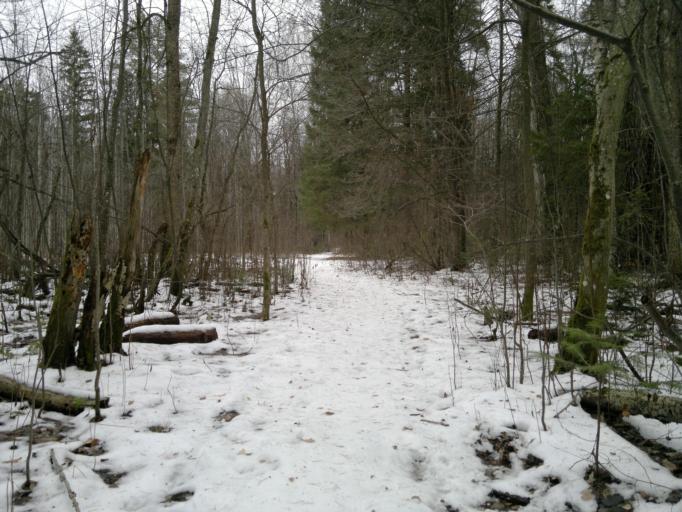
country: RU
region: Mariy-El
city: Yoshkar-Ola
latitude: 56.6118
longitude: 47.9376
